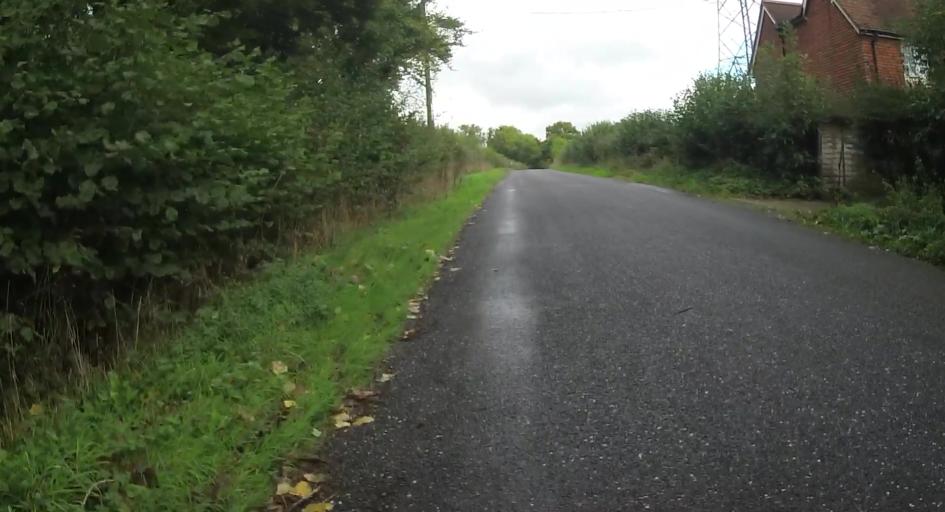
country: GB
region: England
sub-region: Hampshire
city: Tadley
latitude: 51.3183
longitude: -1.1594
